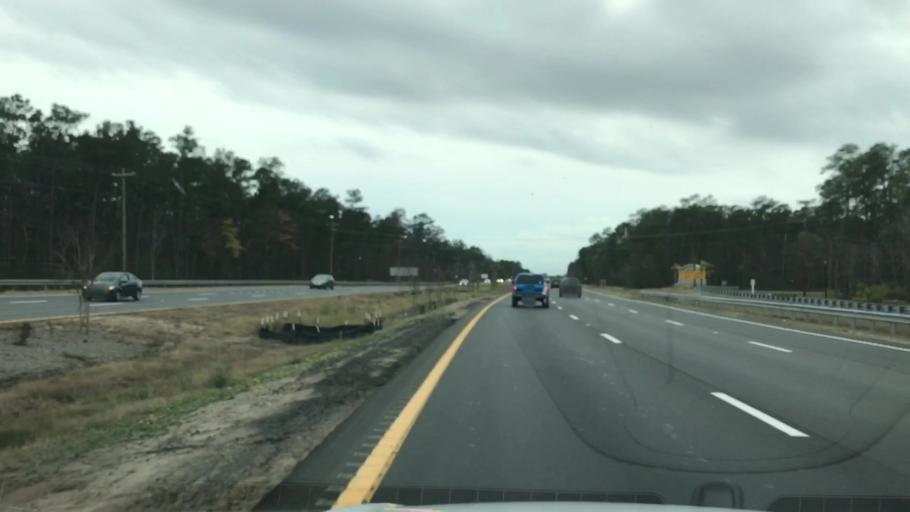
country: US
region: South Carolina
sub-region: Horry County
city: Garden City
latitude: 33.6174
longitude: -79.0070
